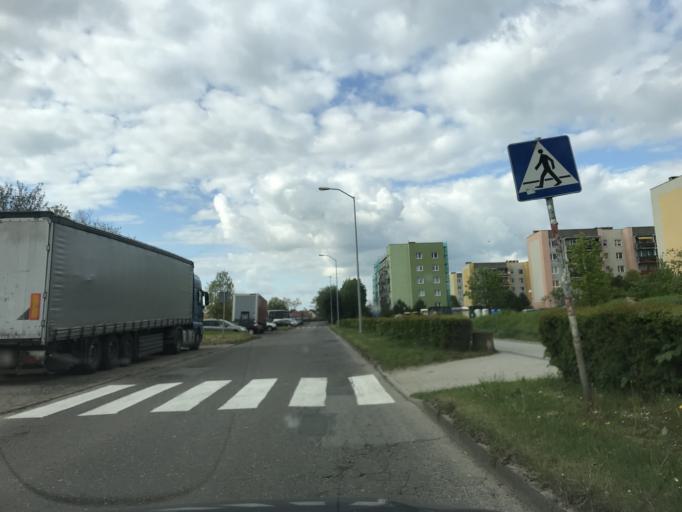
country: PL
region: West Pomeranian Voivodeship
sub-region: Powiat mysliborski
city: Mysliborz
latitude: 52.9256
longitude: 14.8762
